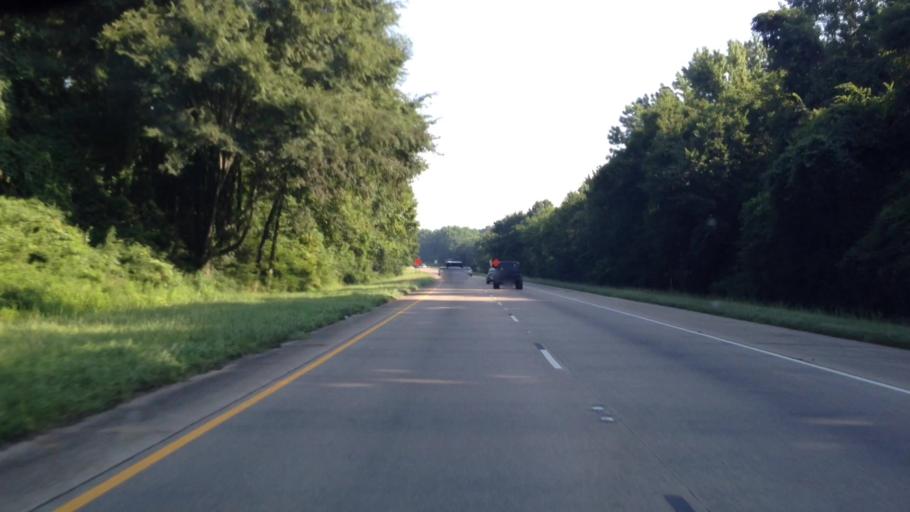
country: US
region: Louisiana
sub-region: Ascension Parish
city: Prairieville
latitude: 30.3025
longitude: -90.9926
